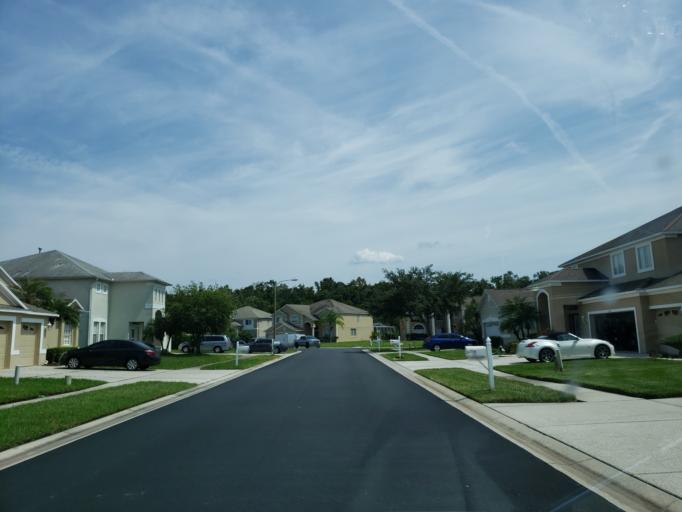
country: US
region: Florida
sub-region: Pasco County
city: Wesley Chapel
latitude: 28.2245
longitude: -82.3918
